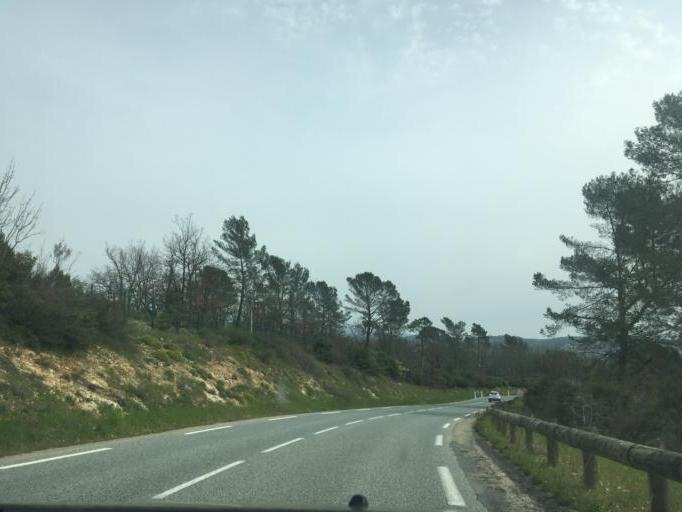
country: FR
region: Provence-Alpes-Cote d'Azur
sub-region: Departement du Var
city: Callian
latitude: 43.5918
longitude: 6.7377
